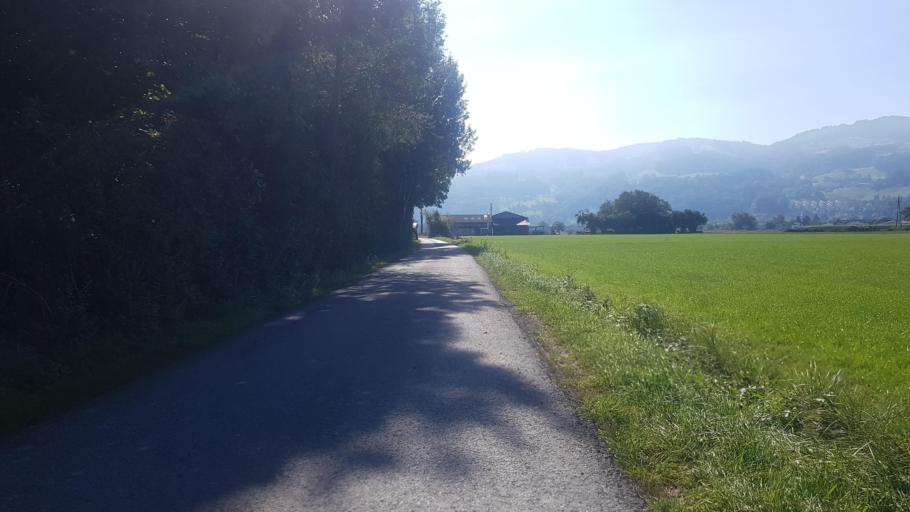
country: AT
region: Vorarlberg
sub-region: Politischer Bezirk Bregenz
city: Gaissau
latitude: 47.4796
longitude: 9.5974
